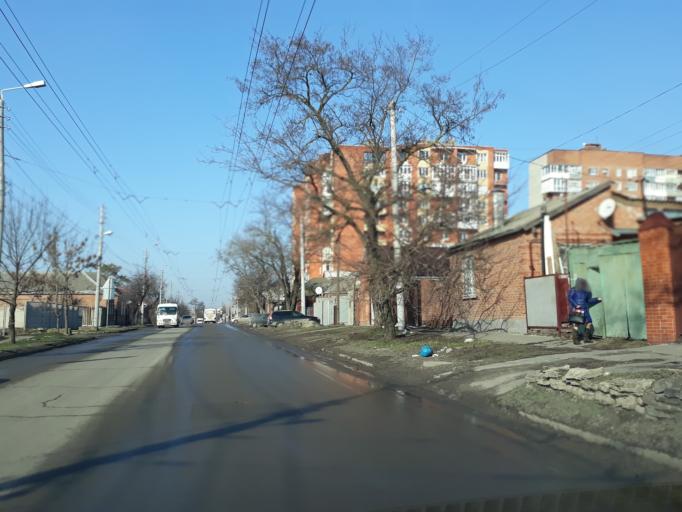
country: RU
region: Rostov
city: Taganrog
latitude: 47.2014
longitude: 38.9076
